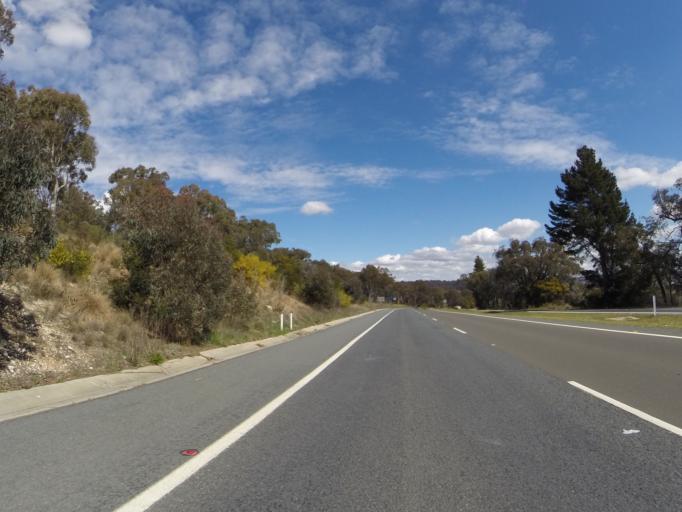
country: AU
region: New South Wales
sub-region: Goulburn Mulwaree
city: Goulburn
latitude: -34.7450
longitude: 149.7566
